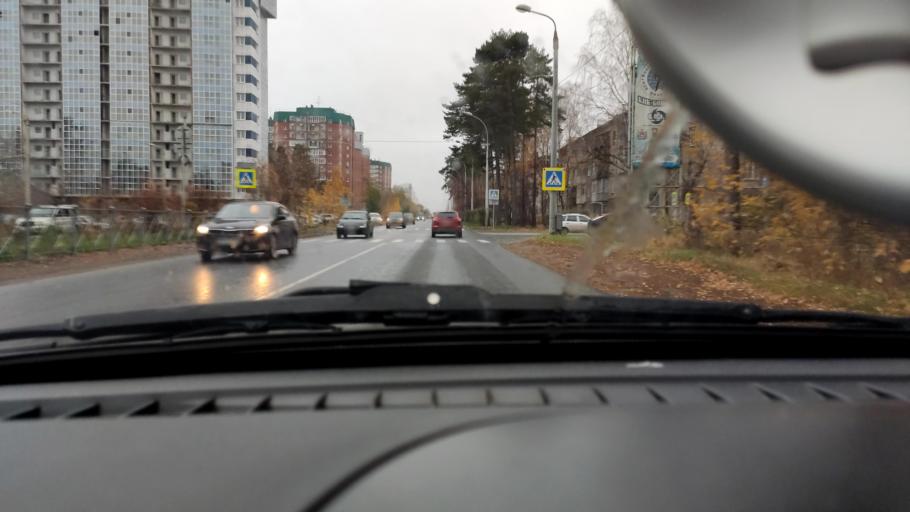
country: RU
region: Perm
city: Kultayevo
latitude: 58.0062
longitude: 55.9690
